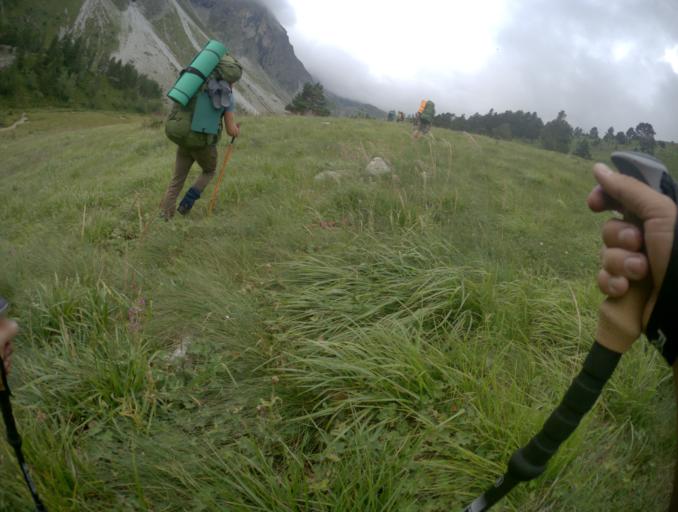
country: RU
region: Karachayevo-Cherkesiya
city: Uchkulan
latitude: 43.3375
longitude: 42.1290
